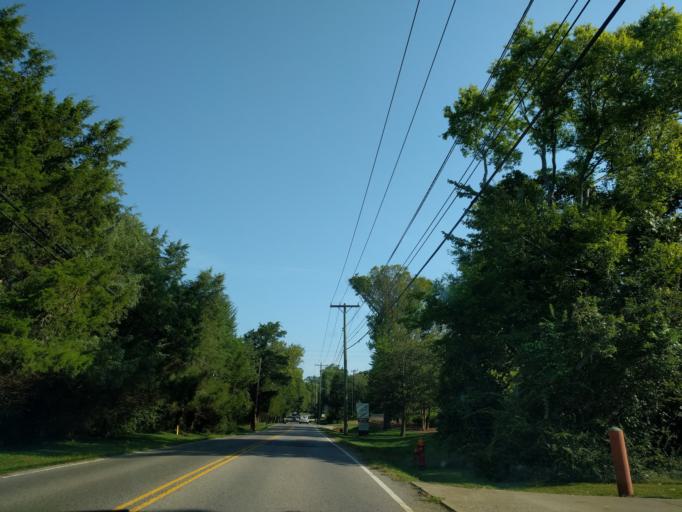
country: US
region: Tennessee
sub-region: Davidson County
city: Forest Hills
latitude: 36.0483
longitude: -86.8161
